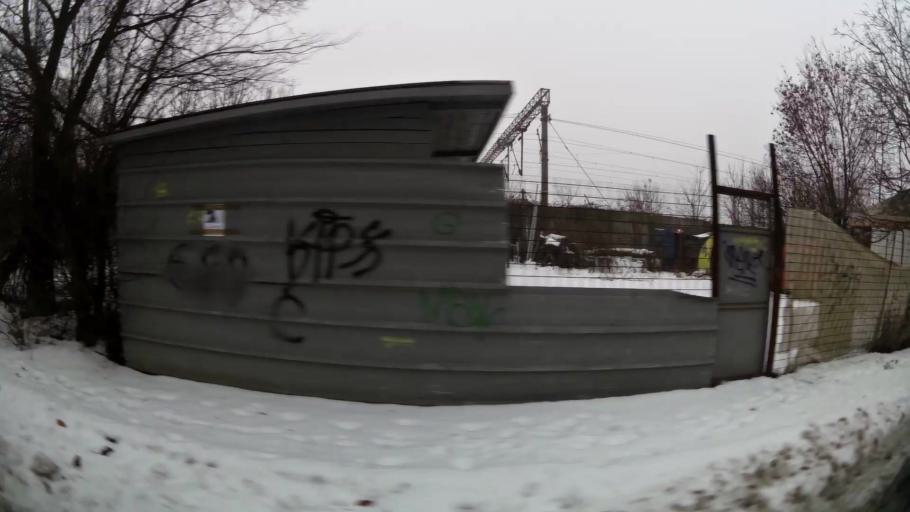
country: RO
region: Ilfov
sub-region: Comuna Chiajna
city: Rosu
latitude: 44.4744
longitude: 26.0322
